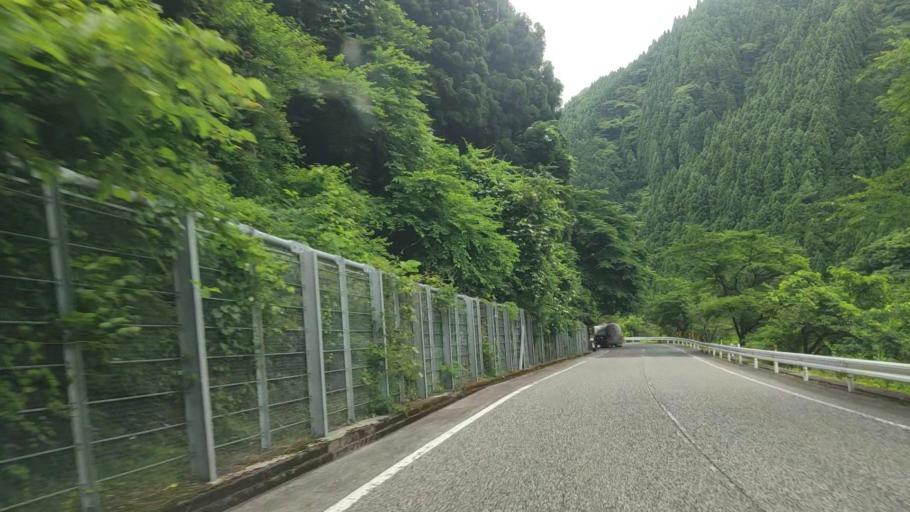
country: JP
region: Tottori
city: Yonago
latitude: 35.2536
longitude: 133.4387
